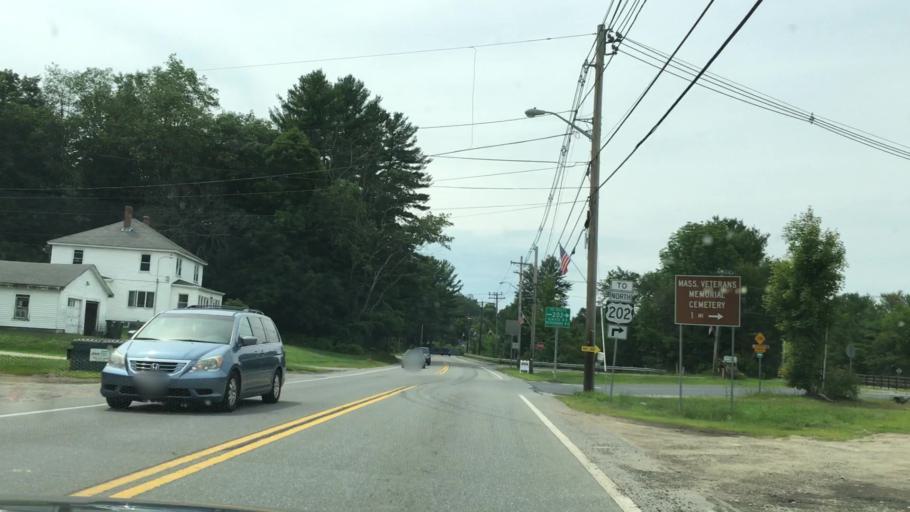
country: US
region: Massachusetts
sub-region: Worcester County
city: Winchendon
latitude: 42.6780
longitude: -72.0317
